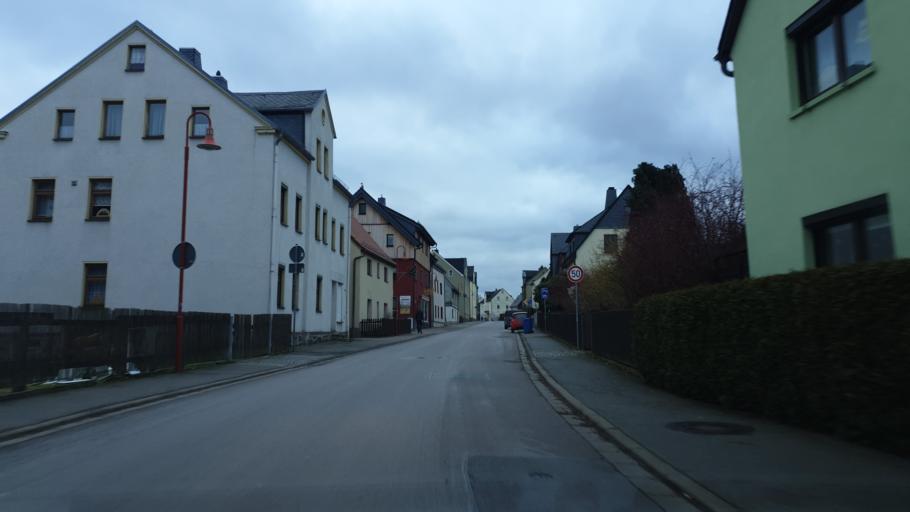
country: DE
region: Saxony
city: Hohndorf
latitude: 50.7394
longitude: 12.6607
